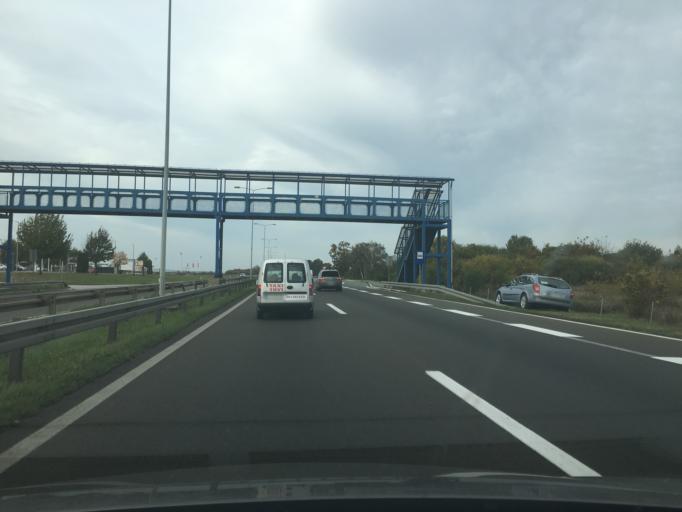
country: RS
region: Central Serbia
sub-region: Belgrade
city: Surcin
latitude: 44.8344
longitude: 20.3115
